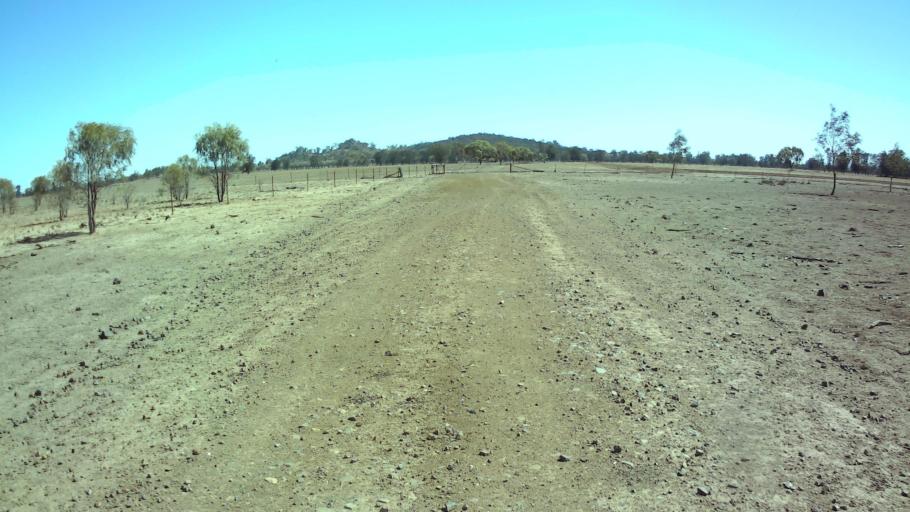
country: AU
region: New South Wales
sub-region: Bland
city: West Wyalong
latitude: -33.7505
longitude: 147.6599
